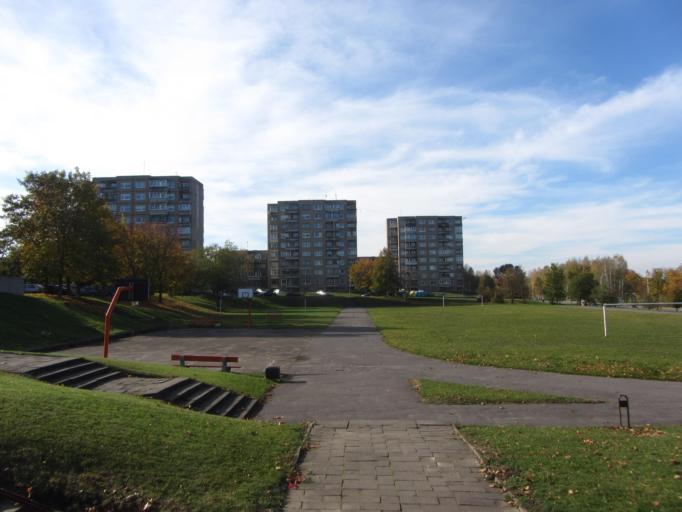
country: LT
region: Vilnius County
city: Elektrenai
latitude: 54.7877
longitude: 24.6785
